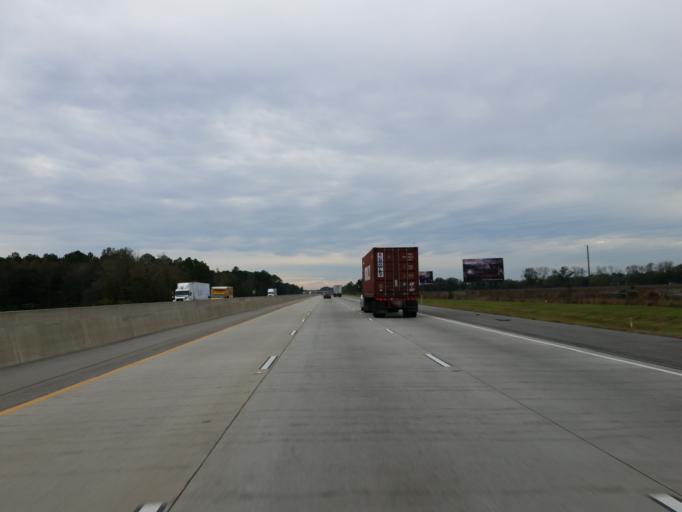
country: US
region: Georgia
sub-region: Tift County
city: Omega
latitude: 31.3107
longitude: -83.4785
